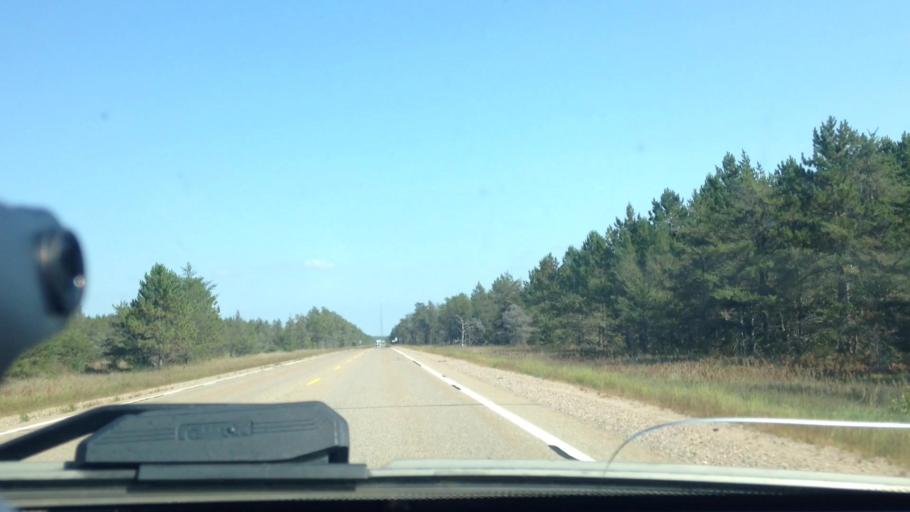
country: US
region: Michigan
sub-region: Chippewa County
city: Sault Ste. Marie
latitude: 46.3587
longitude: -84.8272
